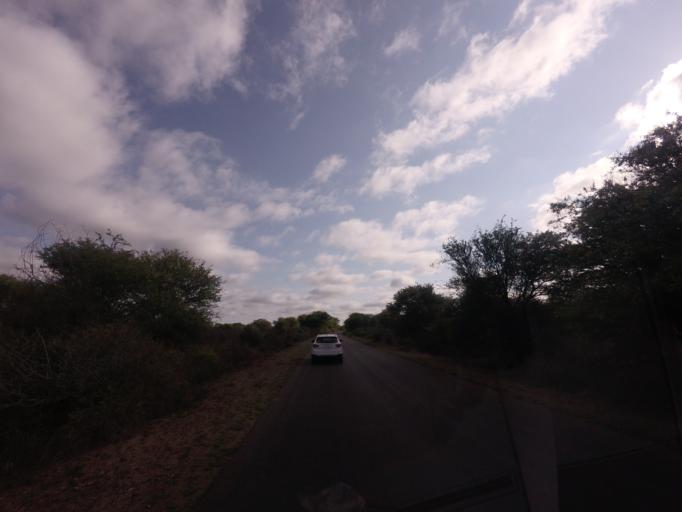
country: ZA
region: Mpumalanga
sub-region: Ehlanzeni District
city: Komatipoort
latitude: -25.2159
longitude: 31.8663
